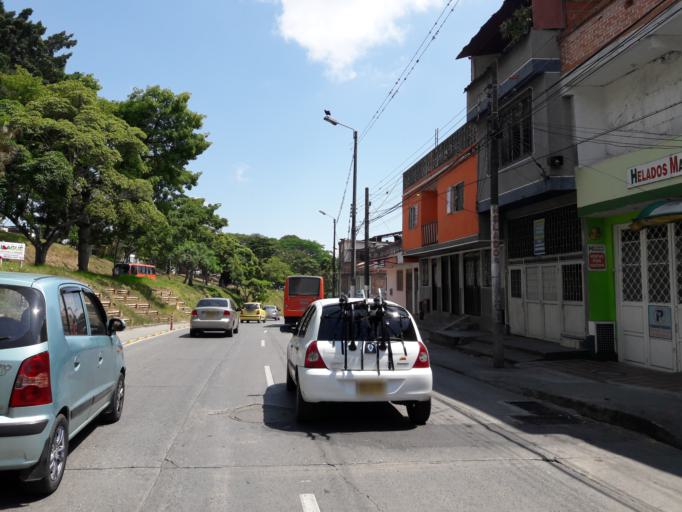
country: CO
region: Tolima
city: Ibague
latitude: 4.4365
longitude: -75.2224
